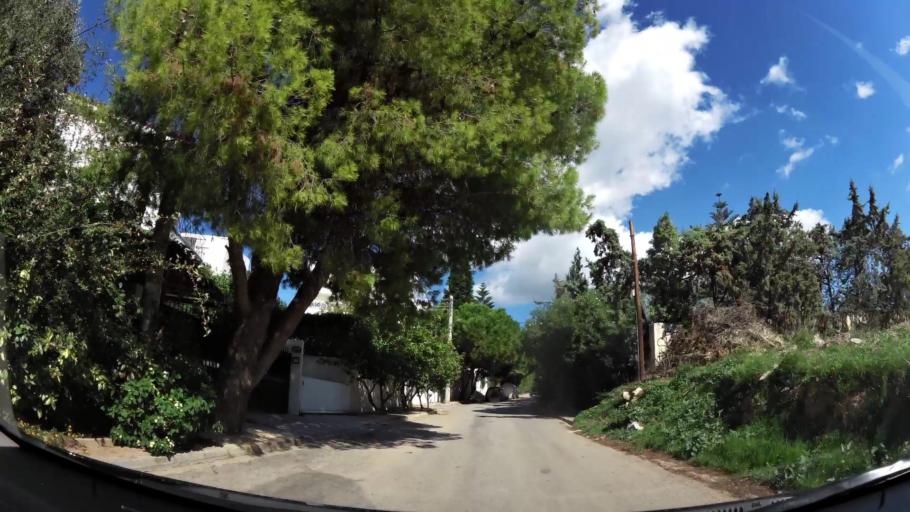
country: GR
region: Attica
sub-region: Nomarchia Anatolikis Attikis
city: Voula
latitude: 37.8378
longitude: 23.7846
